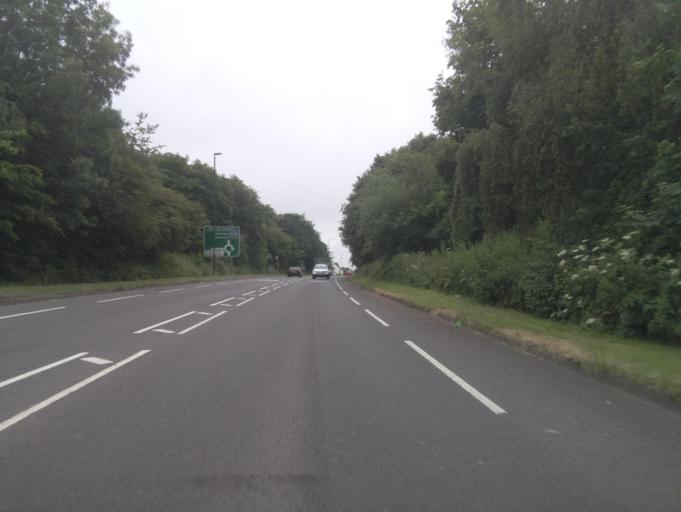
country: GB
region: England
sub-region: Derbyshire
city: Swadlincote
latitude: 52.7688
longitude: -1.5935
